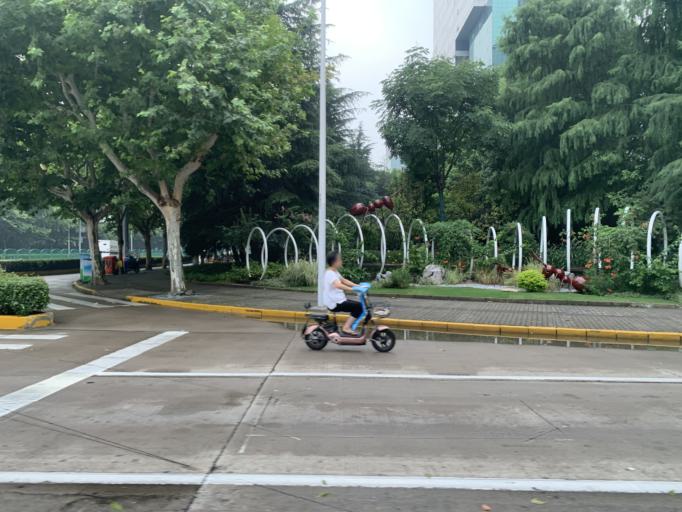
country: CN
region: Shanghai Shi
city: Huamu
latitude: 31.2251
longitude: 121.5463
